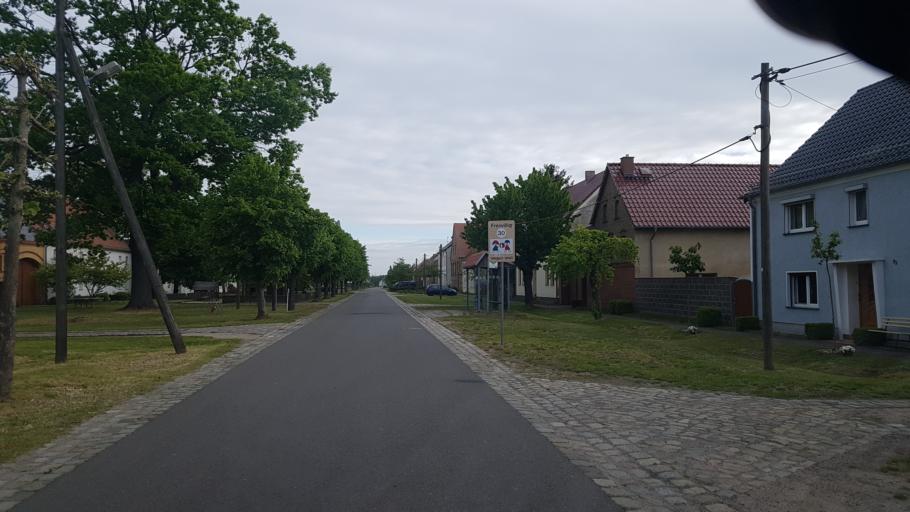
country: DE
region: Brandenburg
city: Luckenwalde
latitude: 52.1090
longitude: 13.1086
